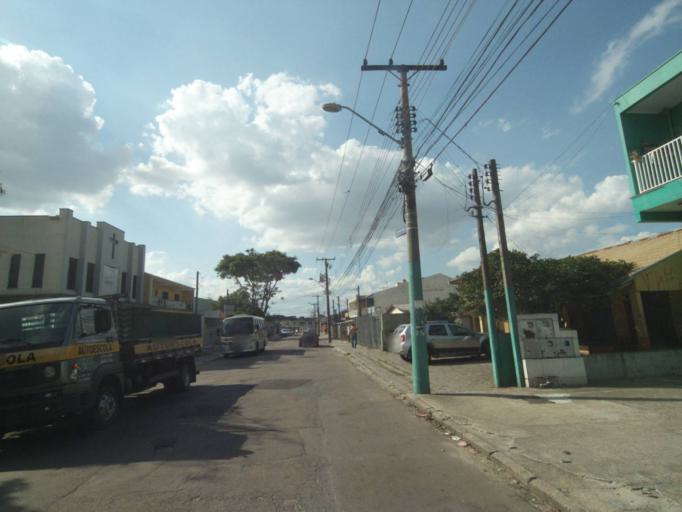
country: BR
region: Parana
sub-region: Sao Jose Dos Pinhais
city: Sao Jose dos Pinhais
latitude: -25.5336
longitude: -49.2701
